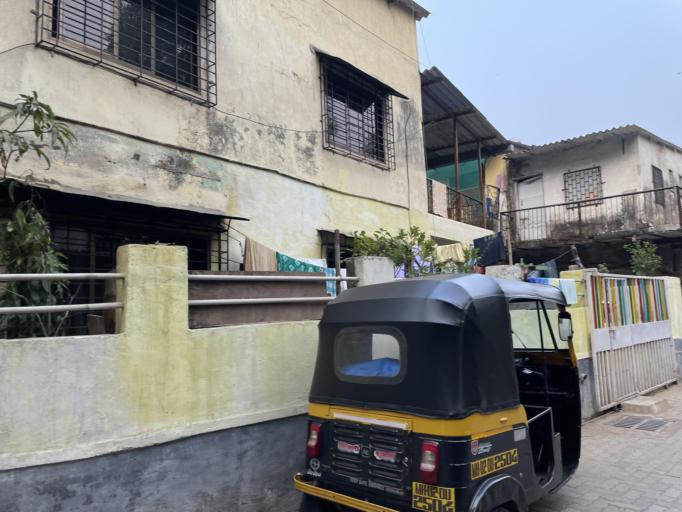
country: IN
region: Maharashtra
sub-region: Mumbai Suburban
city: Borivli
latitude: 19.2385
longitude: 72.8431
